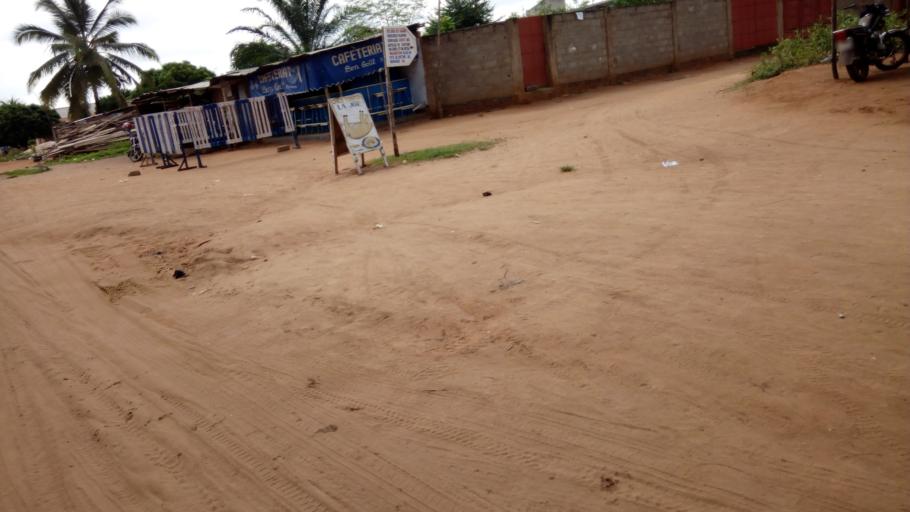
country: TG
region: Maritime
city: Lome
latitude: 6.2224
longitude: 1.1590
